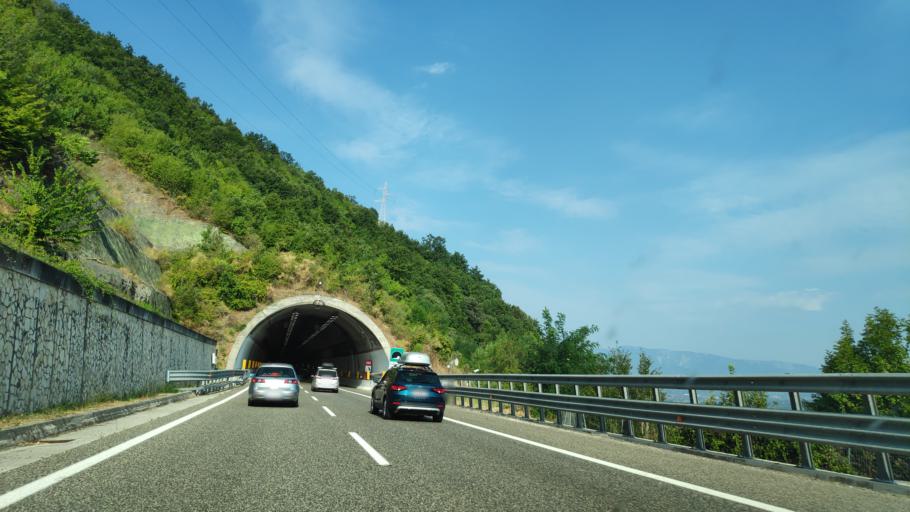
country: IT
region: Campania
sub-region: Provincia di Salerno
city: Petina
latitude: 40.5658
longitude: 15.3758
